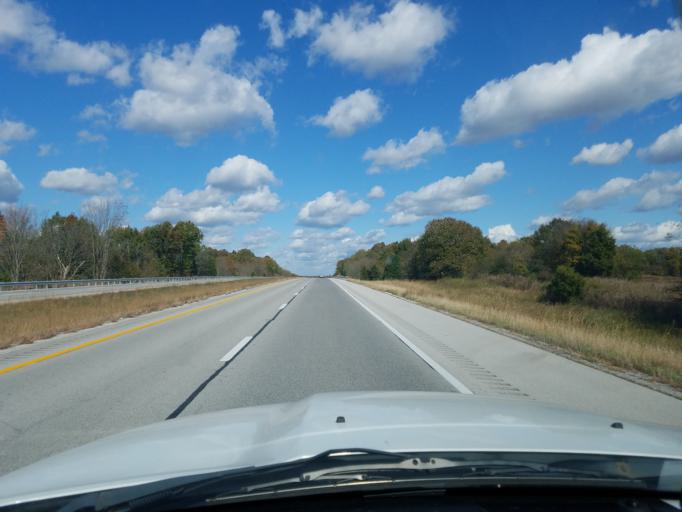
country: US
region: Kentucky
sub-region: Butler County
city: Morgantown
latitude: 37.1099
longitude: -86.6407
